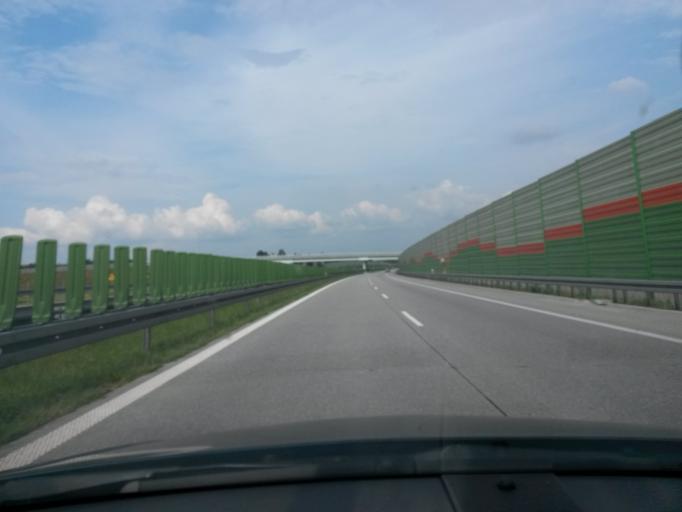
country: PL
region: Lodz Voivodeship
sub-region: Powiat tomaszowski
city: Tomaszow Mazowiecki
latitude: 51.5433
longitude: 19.9697
